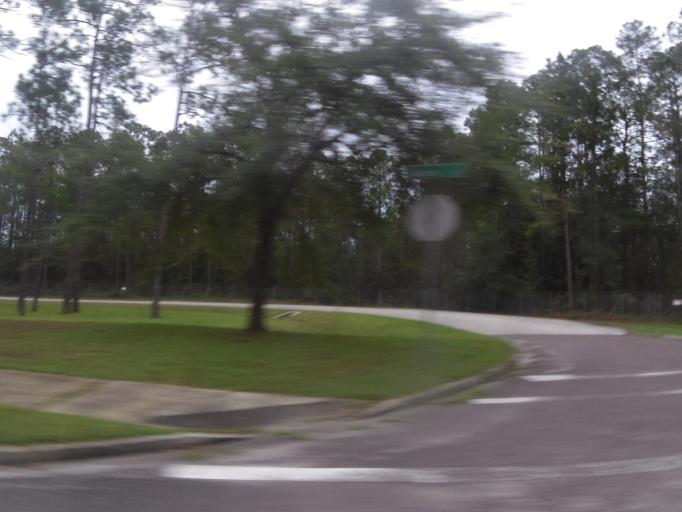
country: US
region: Florida
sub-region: Duval County
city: Baldwin
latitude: 30.2449
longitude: -81.8831
